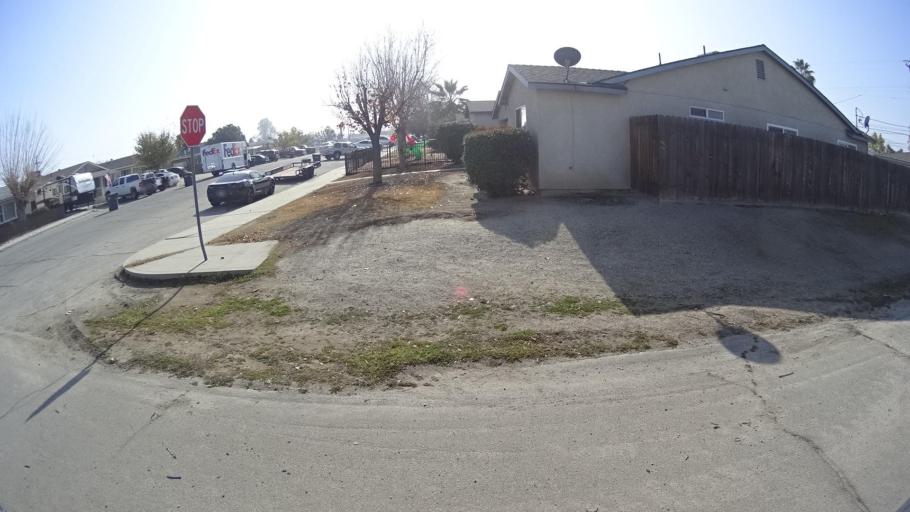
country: US
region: California
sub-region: Kern County
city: Ford City
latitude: 35.1576
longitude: -119.4605
